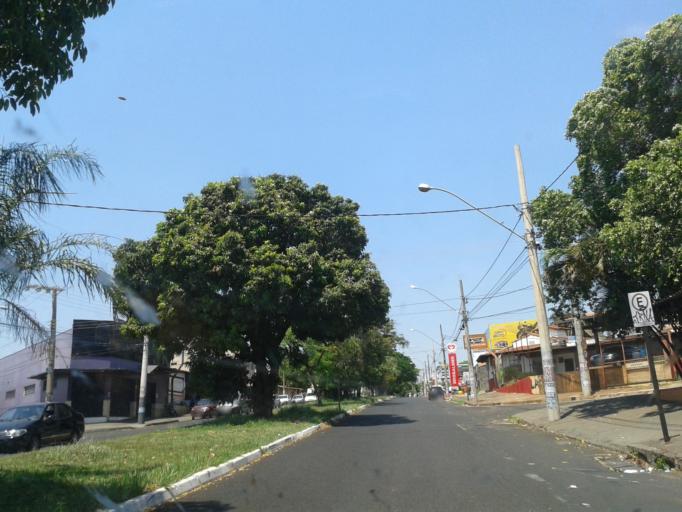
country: BR
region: Minas Gerais
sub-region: Uberlandia
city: Uberlandia
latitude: -18.9305
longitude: -48.3015
